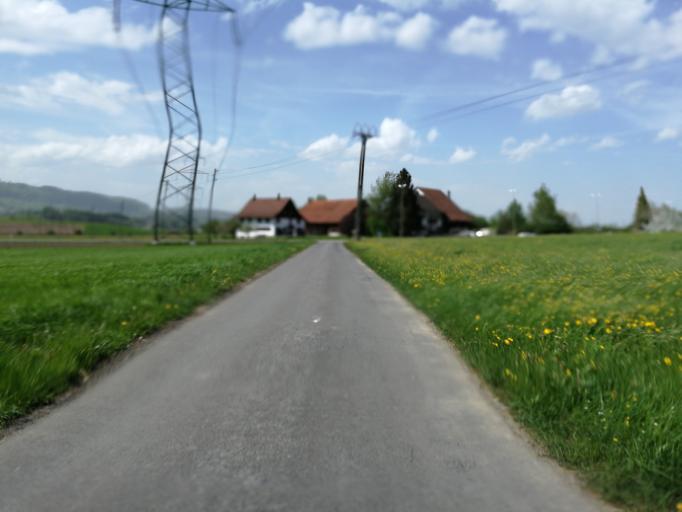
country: CH
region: Zurich
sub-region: Bezirk Meilen
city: Oetwil am See
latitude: 47.2864
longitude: 8.7328
